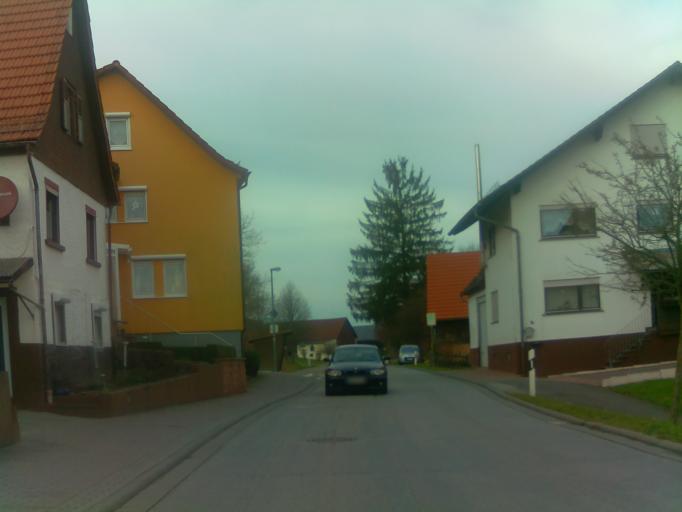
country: DE
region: Hesse
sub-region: Regierungsbezirk Darmstadt
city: Erbach
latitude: 49.6540
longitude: 8.9301
